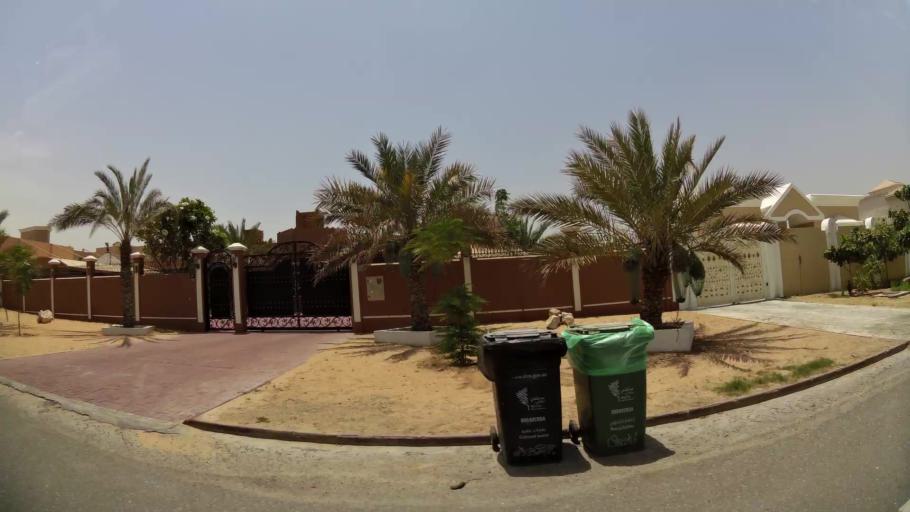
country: AE
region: Ash Shariqah
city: Sharjah
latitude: 25.1978
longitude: 55.3769
